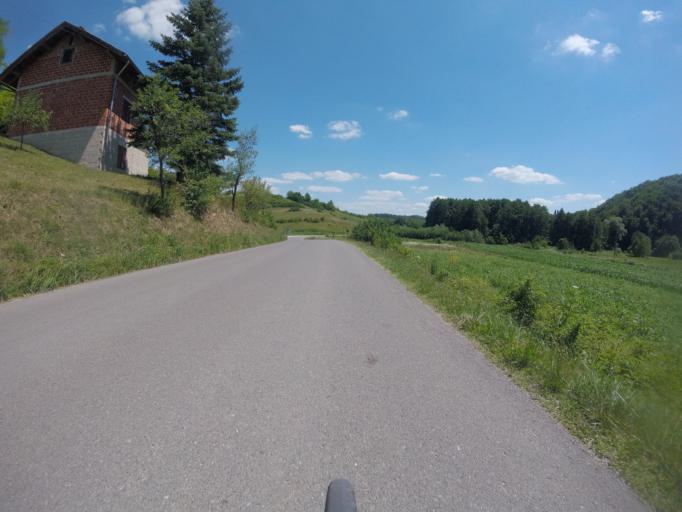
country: HR
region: Karlovacka
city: Ozalj
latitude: 45.6626
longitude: 15.4943
